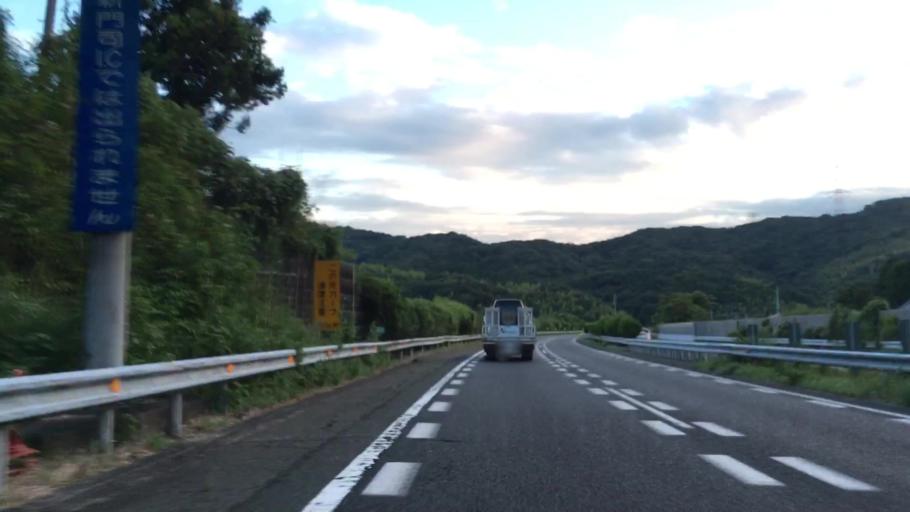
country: JP
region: Yamaguchi
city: Shimonoseki
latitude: 33.9317
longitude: 130.9955
